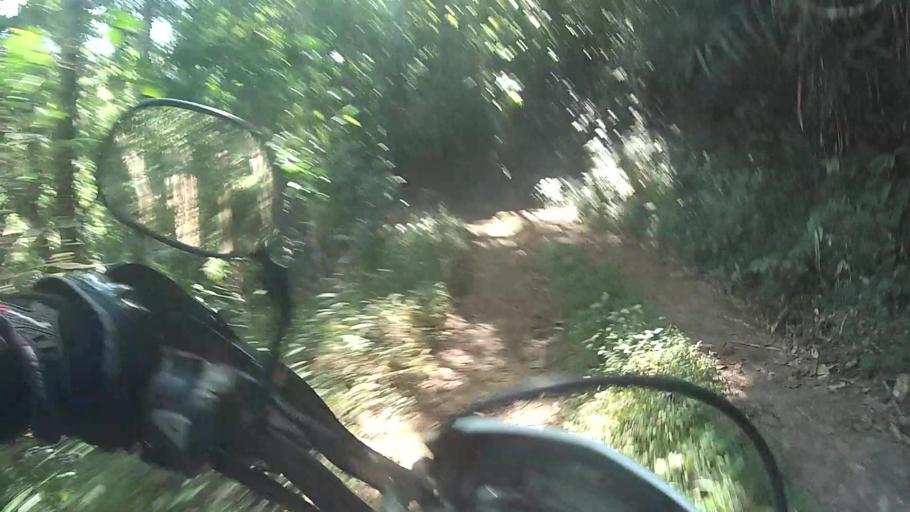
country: TH
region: Chiang Mai
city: Mae On
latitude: 19.0598
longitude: 99.3327
